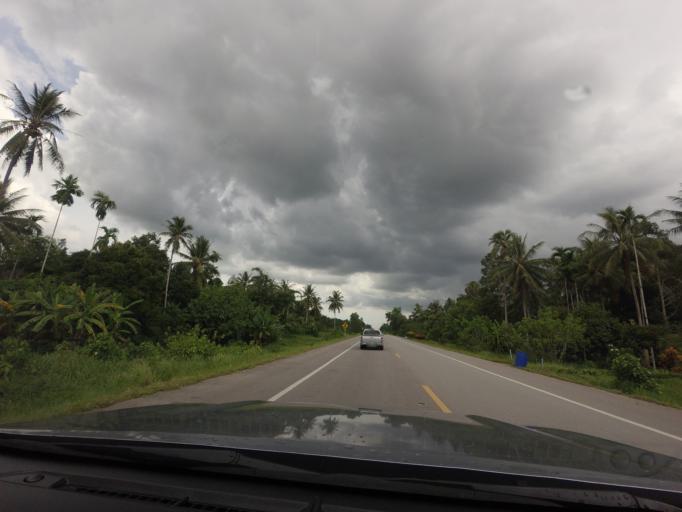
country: TH
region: Chumphon
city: Chumphon
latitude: 10.5458
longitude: 99.1647
